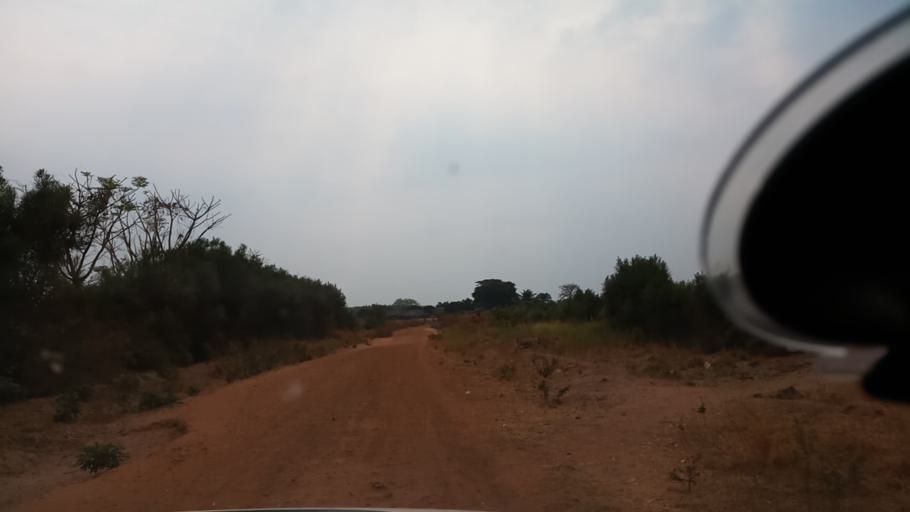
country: ZM
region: Luapula
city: Nchelenge
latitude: -9.0991
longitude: 28.3051
